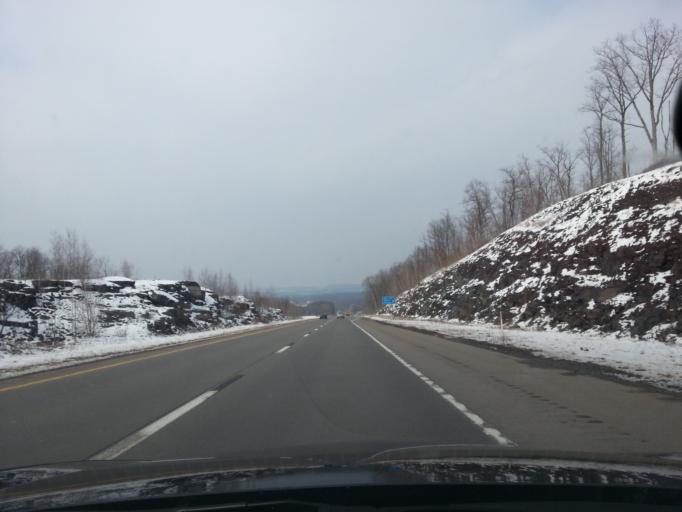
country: US
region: Pennsylvania
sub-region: Luzerne County
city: Freeland
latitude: 41.0940
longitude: -75.9618
